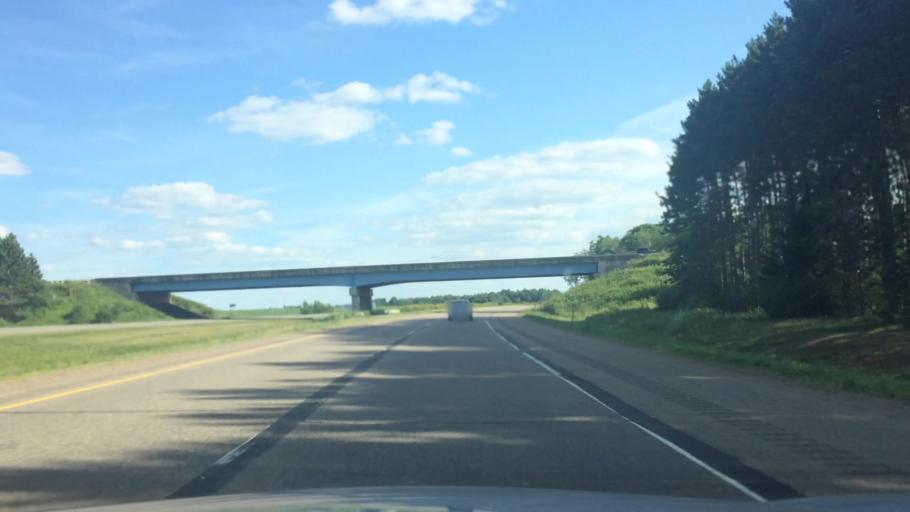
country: US
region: Wisconsin
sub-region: Lincoln County
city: Merrill
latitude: 45.1936
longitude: -89.6470
